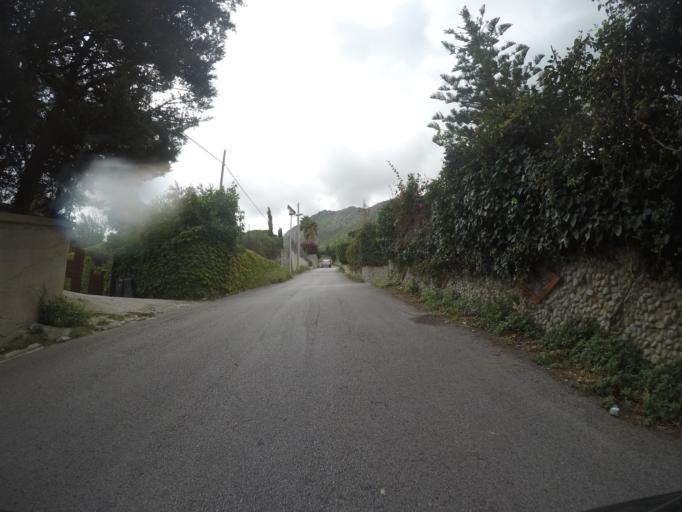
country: IT
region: Sicily
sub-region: Palermo
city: Carini
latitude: 38.1240
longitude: 13.1834
